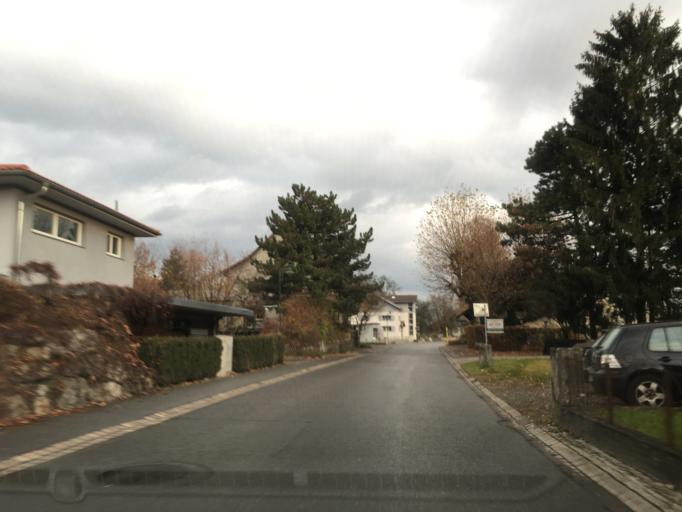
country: AT
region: Vorarlberg
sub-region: Politischer Bezirk Feldkirch
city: Mader
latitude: 47.3455
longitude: 9.6223
